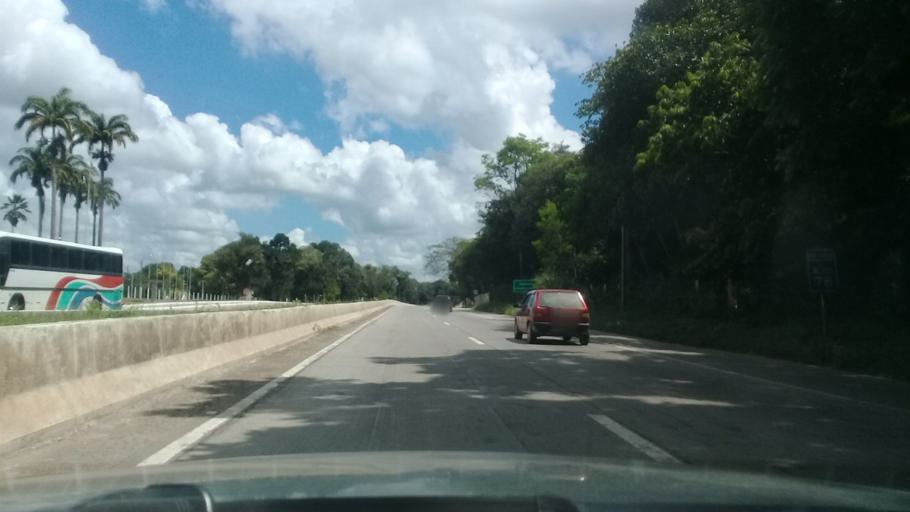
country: BR
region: Pernambuco
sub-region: Carpina
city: Carpina
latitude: -7.9243
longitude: -35.1537
